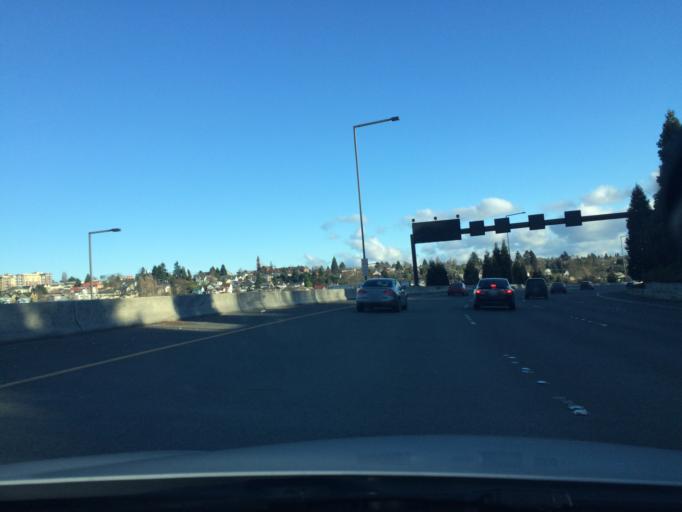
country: US
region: Washington
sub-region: King County
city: Seattle
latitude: 47.5949
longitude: -122.3166
